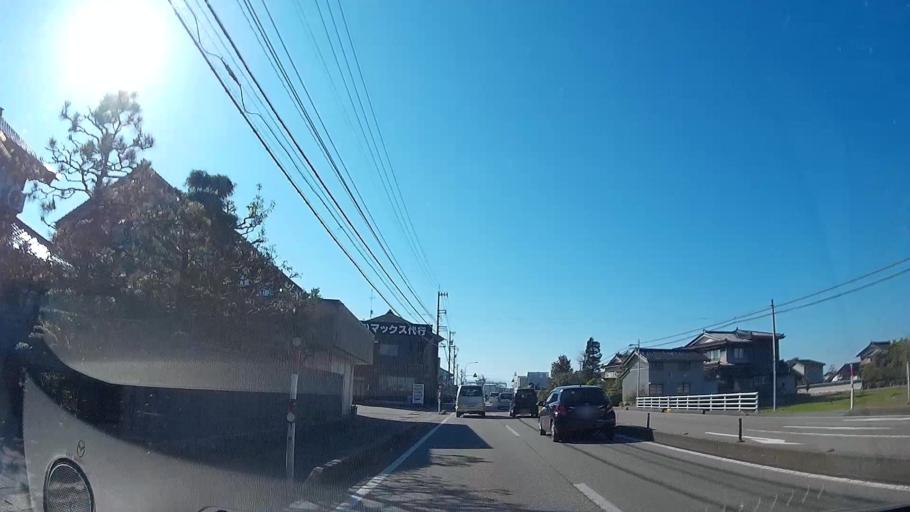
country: JP
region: Toyama
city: Takaoka
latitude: 36.6981
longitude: 136.9842
